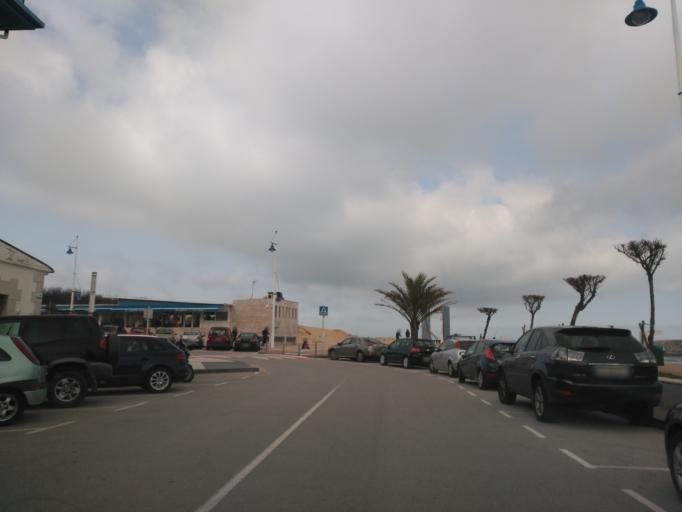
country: ES
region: Cantabria
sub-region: Provincia de Cantabria
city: Suances
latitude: 43.4332
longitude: -4.0358
